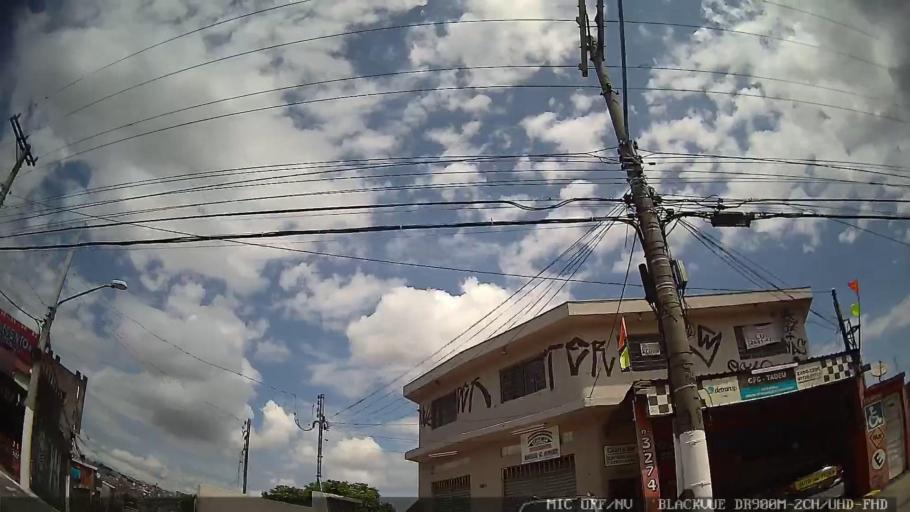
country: BR
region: Sao Paulo
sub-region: Guarulhos
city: Guarulhos
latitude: -23.5194
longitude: -46.4709
